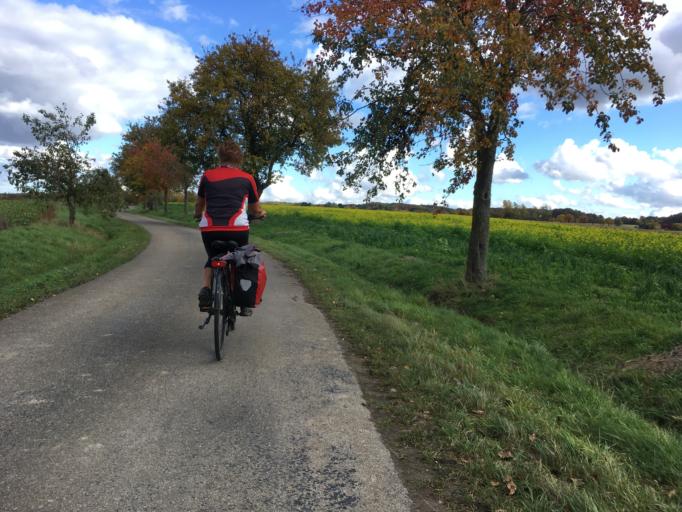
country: DE
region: Baden-Wuerttemberg
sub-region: Regierungsbezirk Stuttgart
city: Untermunkheim
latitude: 49.1855
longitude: 9.7107
